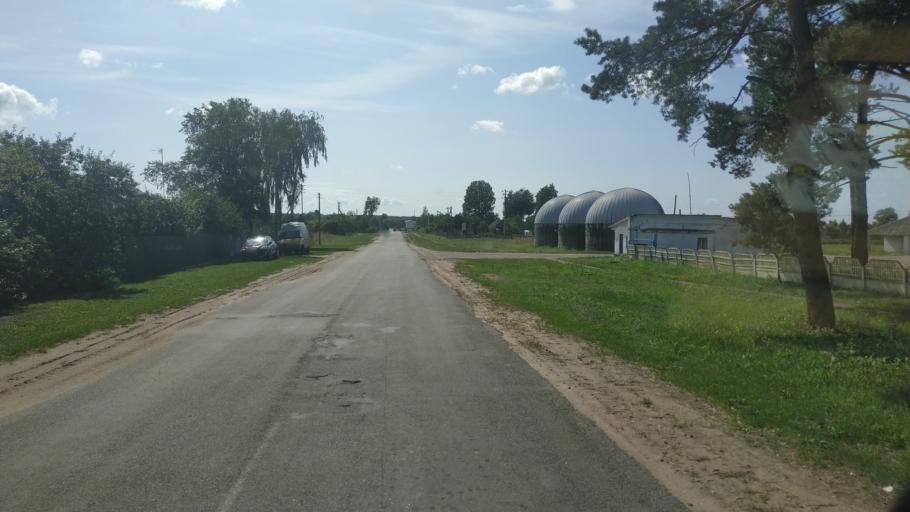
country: BY
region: Mogilev
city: Poselok Voskhod
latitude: 53.7095
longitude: 30.4991
